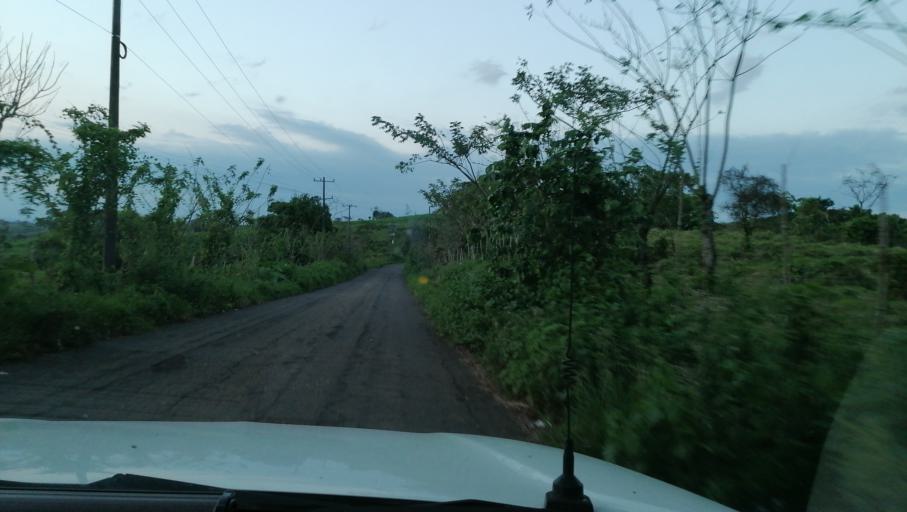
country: MX
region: Chiapas
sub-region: Ostuacan
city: Nuevo Juan del Grijalva
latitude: 17.4350
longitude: -93.3511
